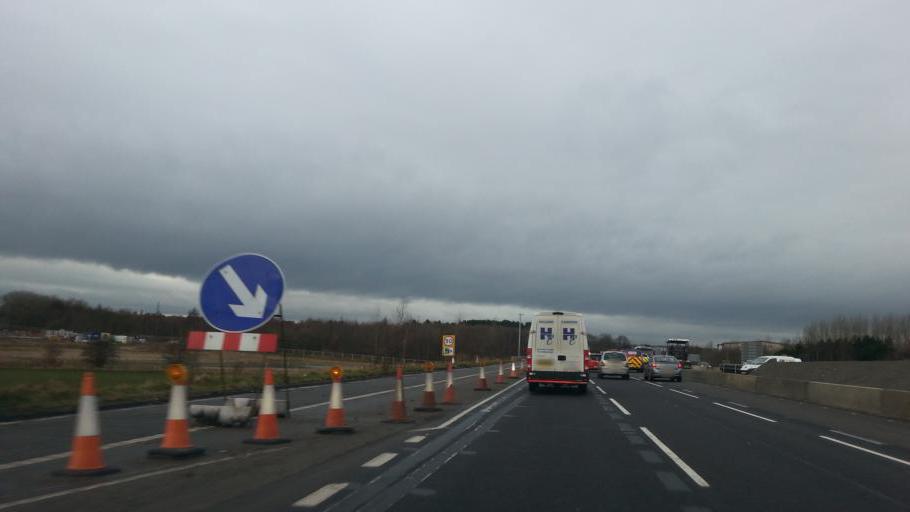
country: GB
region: England
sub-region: City and Borough of Wakefield
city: Normanton
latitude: 53.7092
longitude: -1.4045
